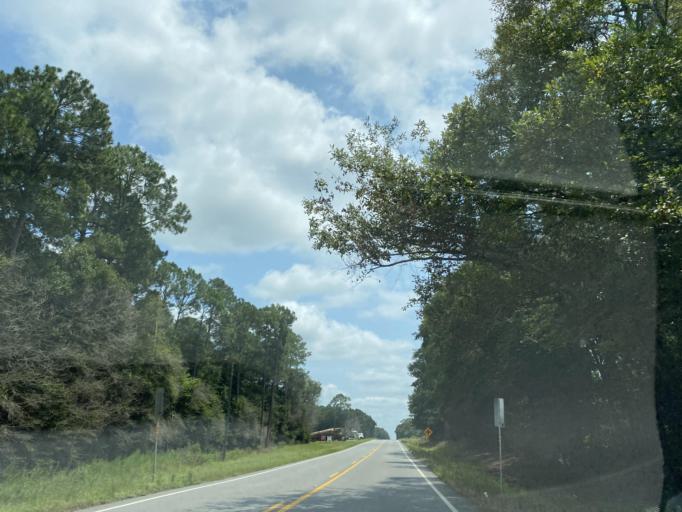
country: US
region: Georgia
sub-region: Jeff Davis County
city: Hazlehurst
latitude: 31.7140
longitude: -82.5211
